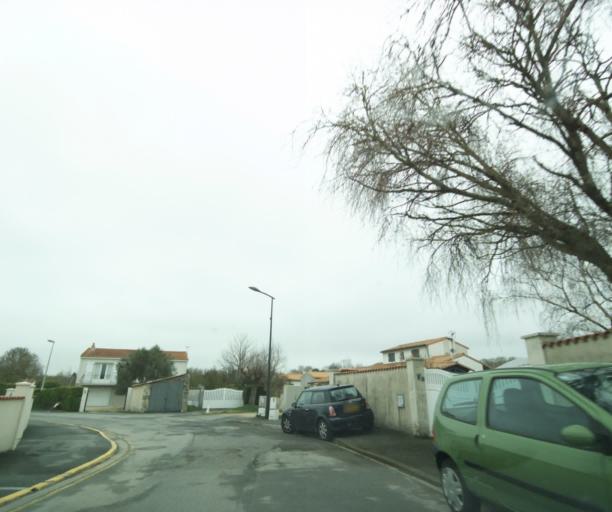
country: FR
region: Poitou-Charentes
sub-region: Departement de la Charente-Maritime
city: Lagord
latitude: 46.1836
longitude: -1.1398
